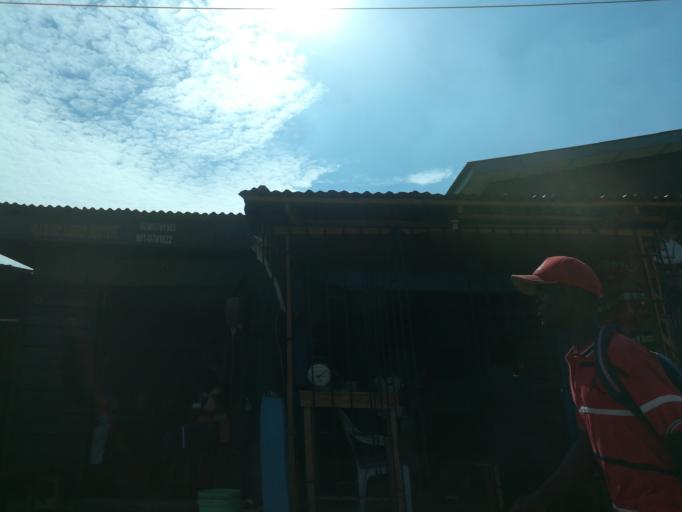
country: NG
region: Lagos
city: Ikorodu
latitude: 6.6015
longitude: 3.5056
